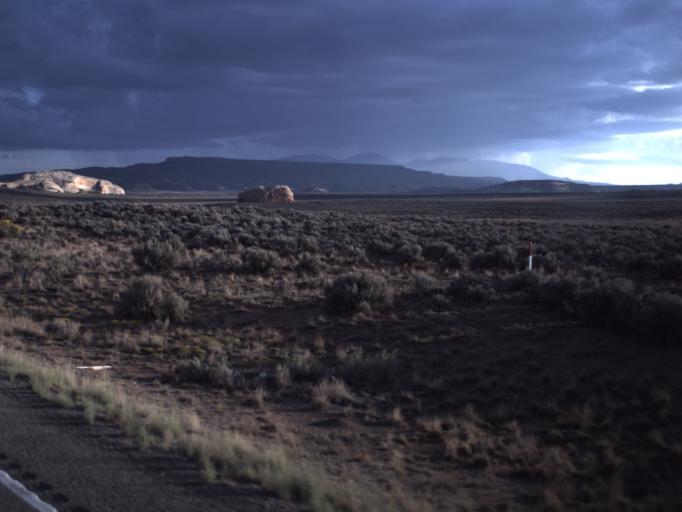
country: US
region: Utah
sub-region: San Juan County
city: Monticello
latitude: 38.0898
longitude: -109.3564
